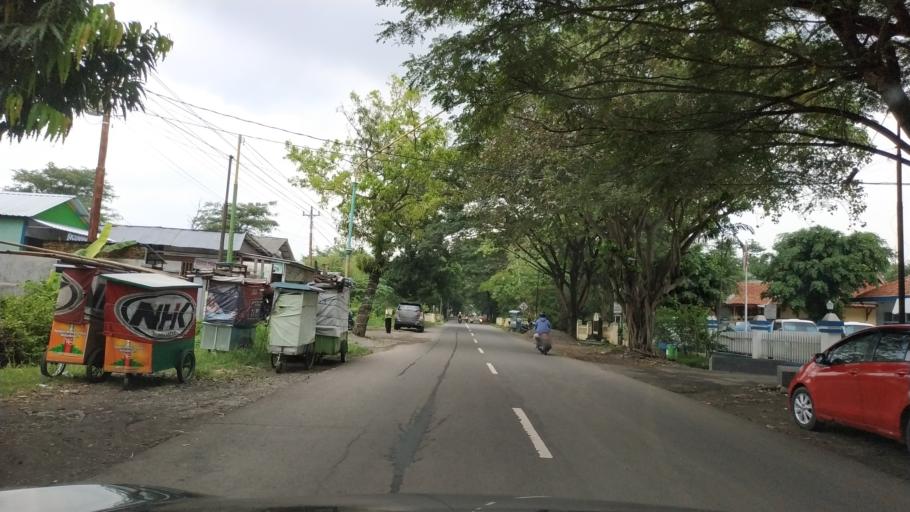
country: ID
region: Central Java
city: Slawi
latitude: -6.9938
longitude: 109.1258
